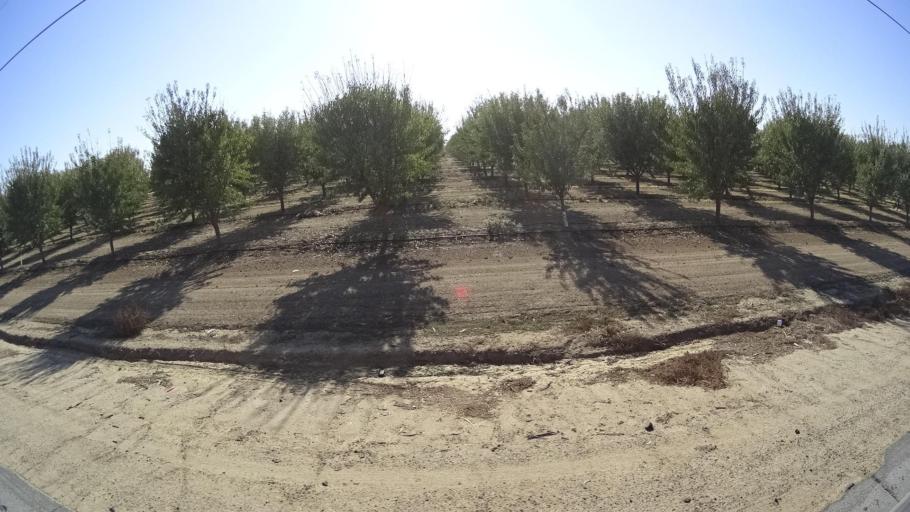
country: US
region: California
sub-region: Kern County
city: McFarland
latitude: 35.7178
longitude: -119.2015
